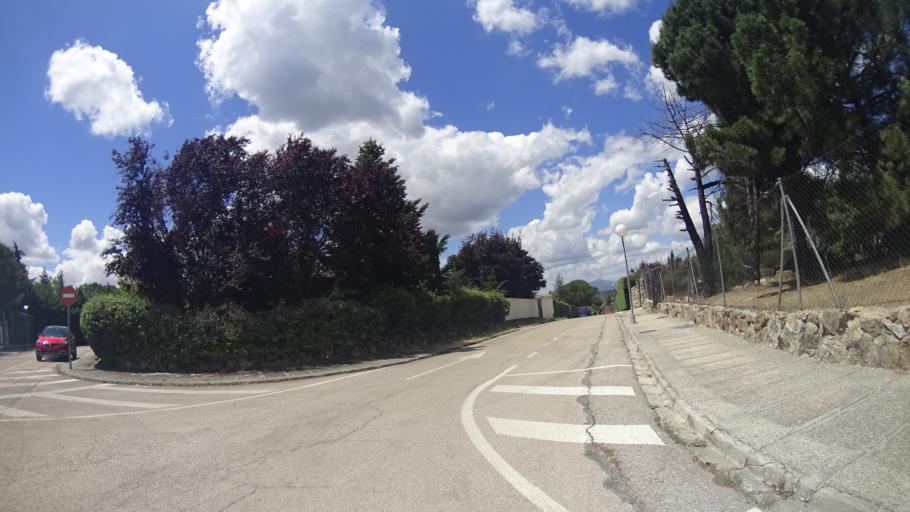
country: ES
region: Madrid
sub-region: Provincia de Madrid
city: Hoyo de Manzanares
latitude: 40.6136
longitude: -3.9296
